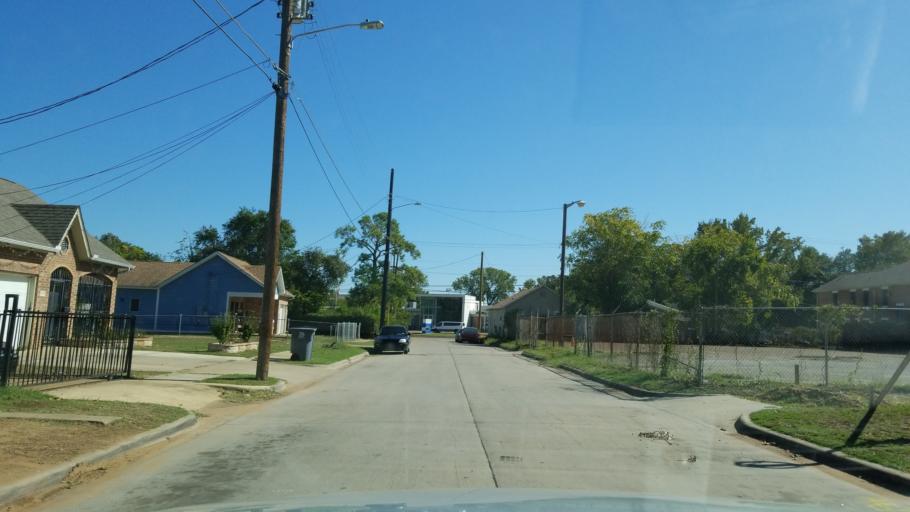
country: US
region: Texas
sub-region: Dallas County
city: Dallas
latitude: 32.7749
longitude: -96.7434
